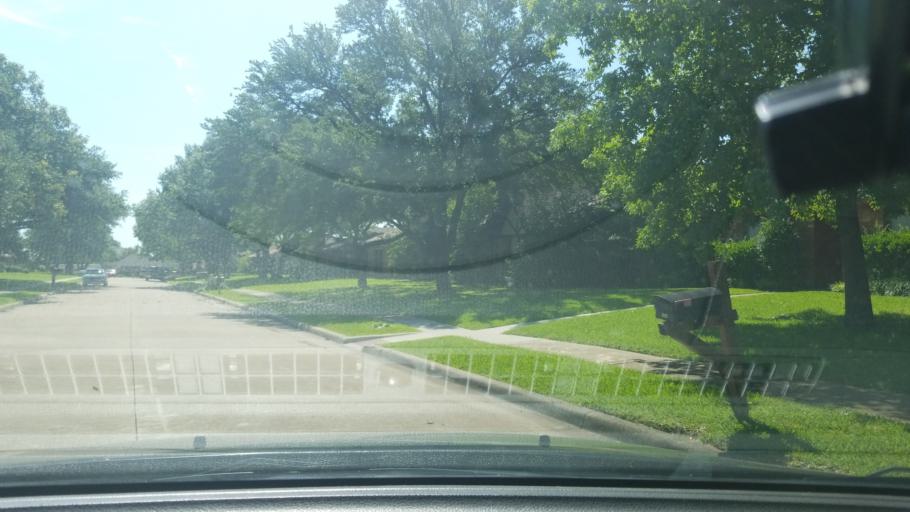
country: US
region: Texas
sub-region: Dallas County
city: Mesquite
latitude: 32.7743
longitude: -96.5939
